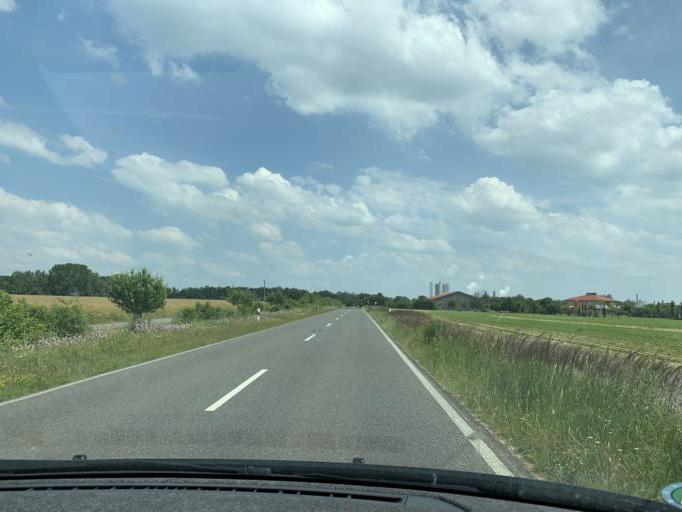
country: DE
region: North Rhine-Westphalia
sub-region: Regierungsbezirk Koln
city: Bergheim
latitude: 51.0023
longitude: 6.6237
